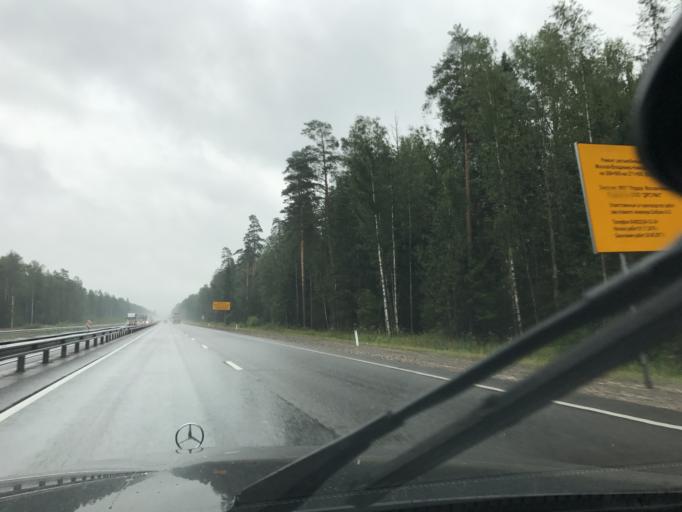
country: RU
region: Vladimir
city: Stepantsevo
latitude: 56.2263
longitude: 41.6408
